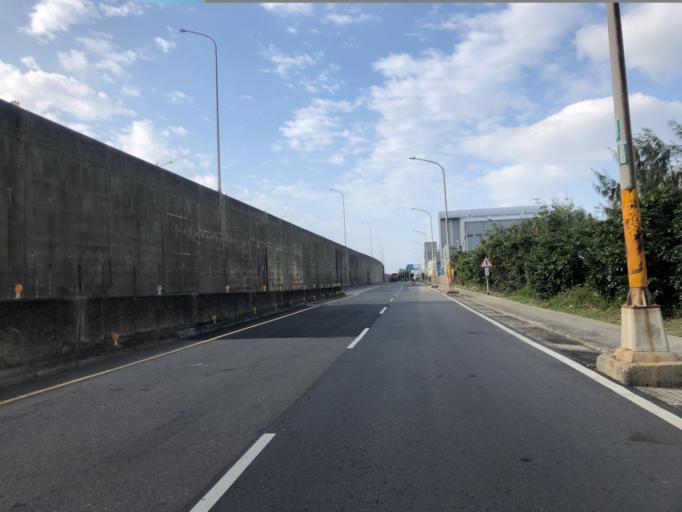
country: TW
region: Taiwan
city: Taoyuan City
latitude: 25.0542
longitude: 121.0932
